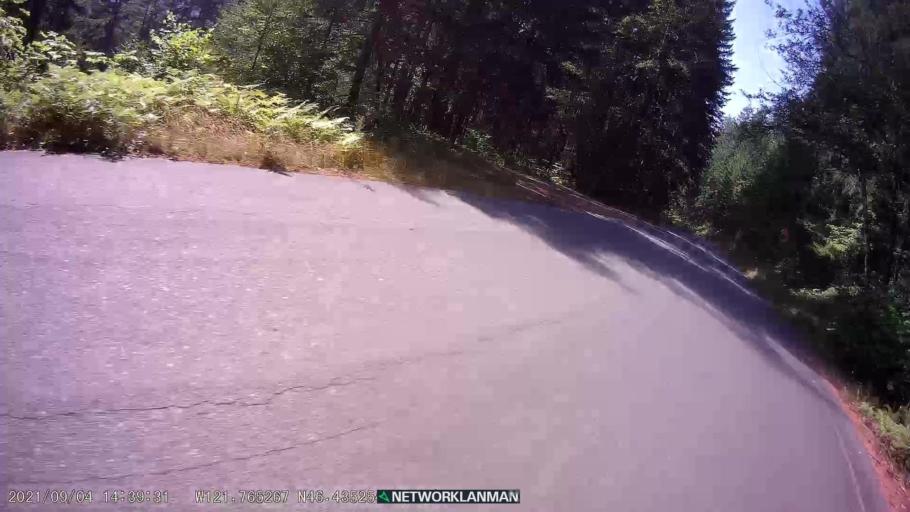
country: US
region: Washington
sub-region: Lewis County
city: Morton
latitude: 46.4354
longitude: -121.7654
